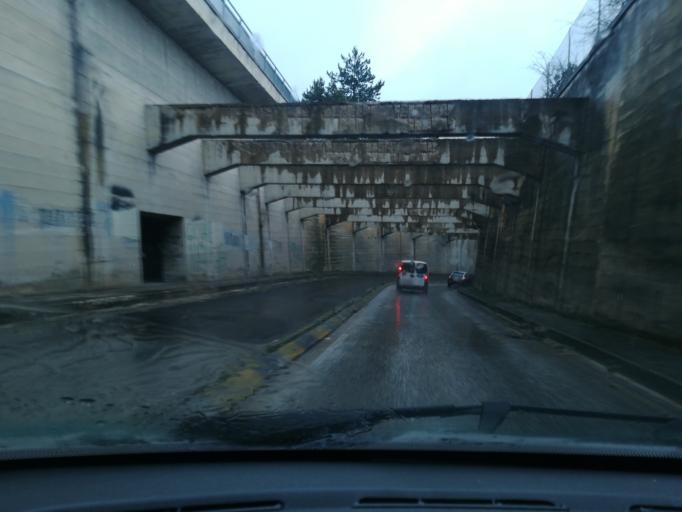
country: IT
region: The Marches
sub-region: Provincia di Macerata
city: Macerata
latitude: 43.2894
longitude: 13.4377
